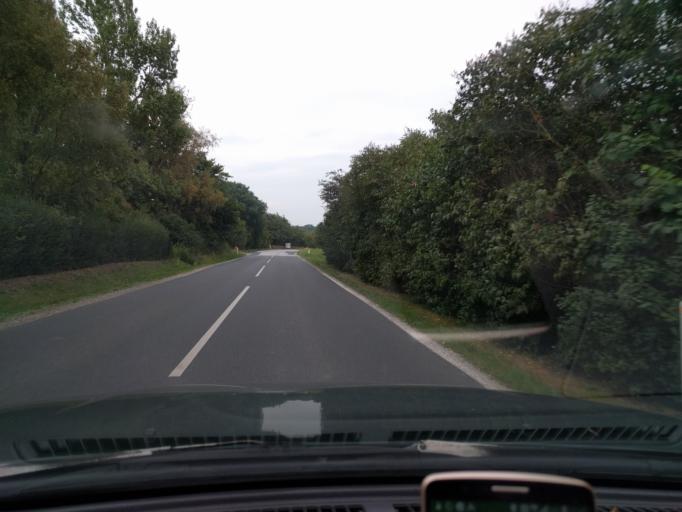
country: DK
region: Zealand
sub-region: Slagelse Kommune
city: Skaelskor
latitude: 55.2922
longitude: 11.2645
